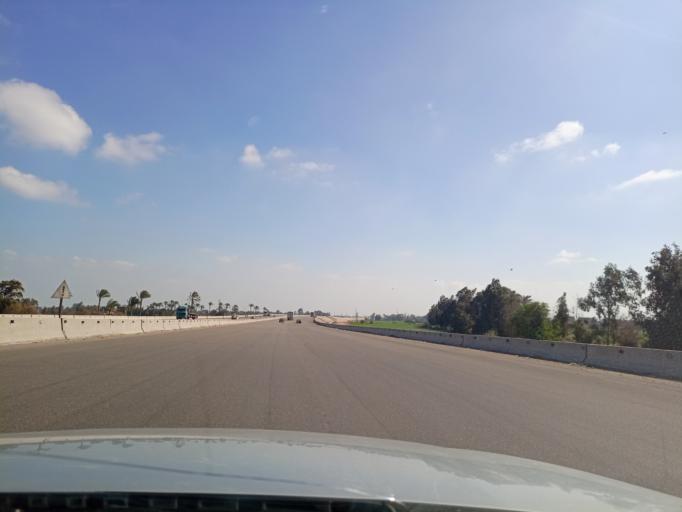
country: EG
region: Eastern Province
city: Mashtul as Suq
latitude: 30.4651
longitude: 31.3103
